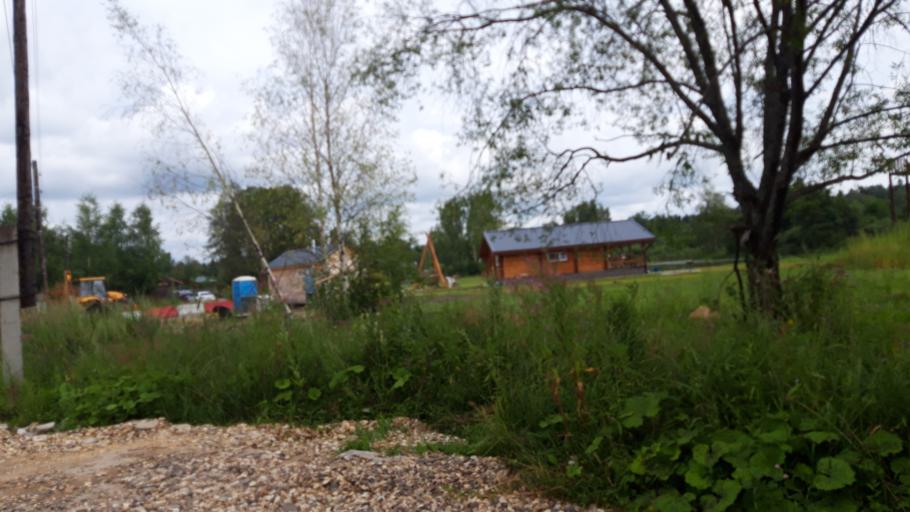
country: RU
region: Tverskaya
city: Konakovo
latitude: 56.6743
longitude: 36.7217
